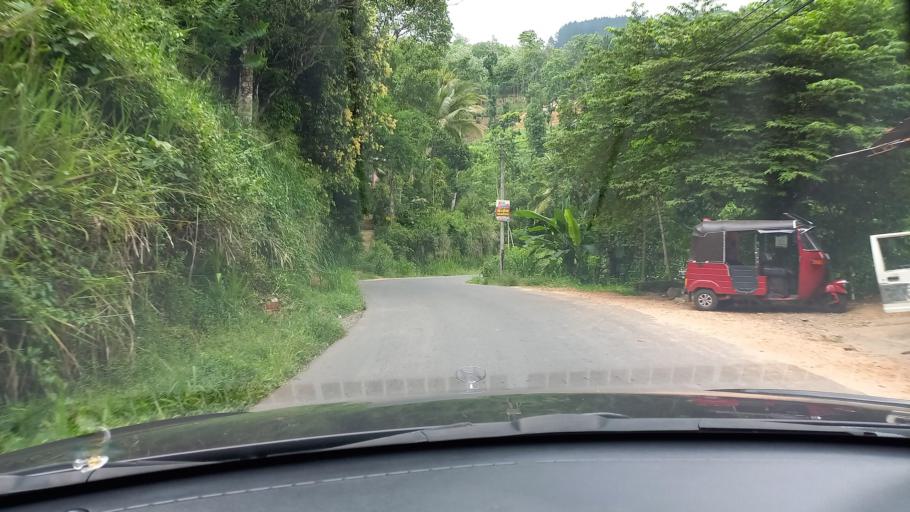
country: LK
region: Central
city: Gampola
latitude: 7.2100
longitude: 80.6235
